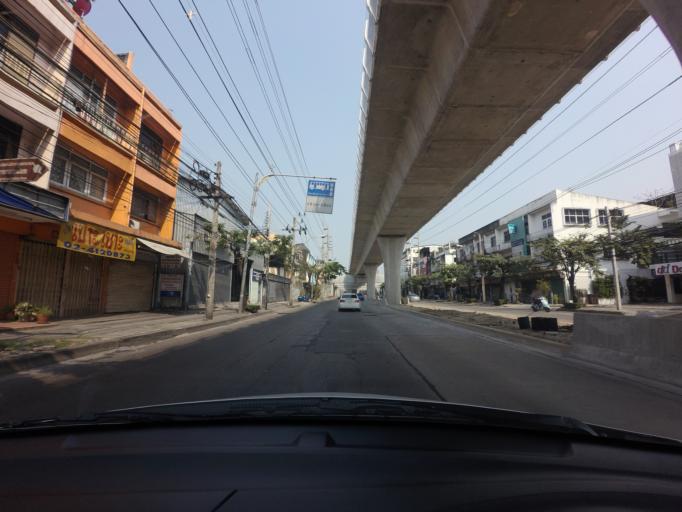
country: TH
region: Bangkok
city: Bangkok Noi
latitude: 13.7497
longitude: 100.4698
